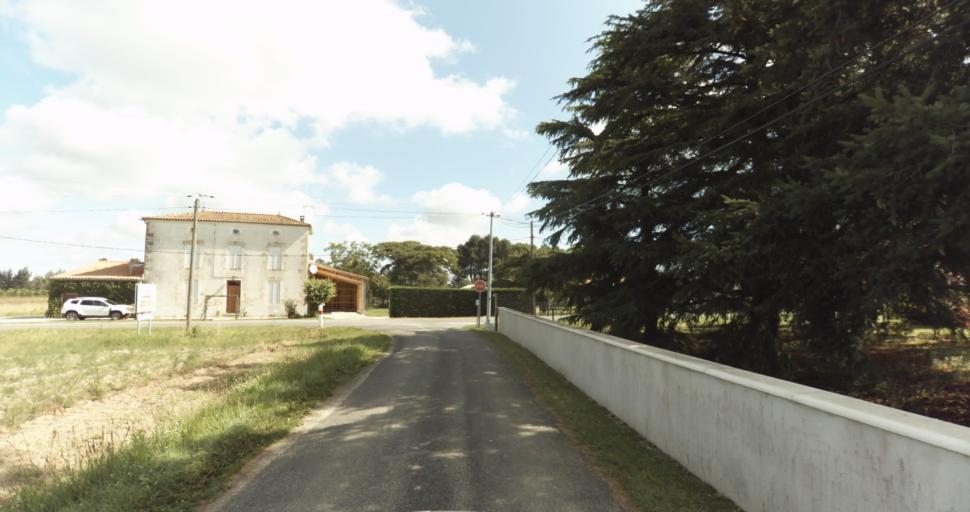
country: FR
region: Aquitaine
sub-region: Departement de la Gironde
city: Bazas
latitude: 44.4407
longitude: -0.1936
